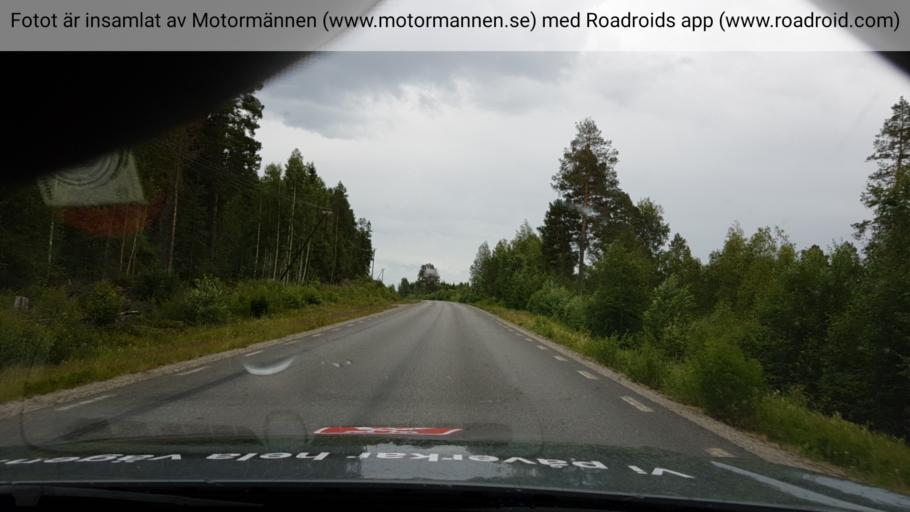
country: SE
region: Jaemtland
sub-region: Braecke Kommun
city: Braecke
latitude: 62.3899
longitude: 15.0468
